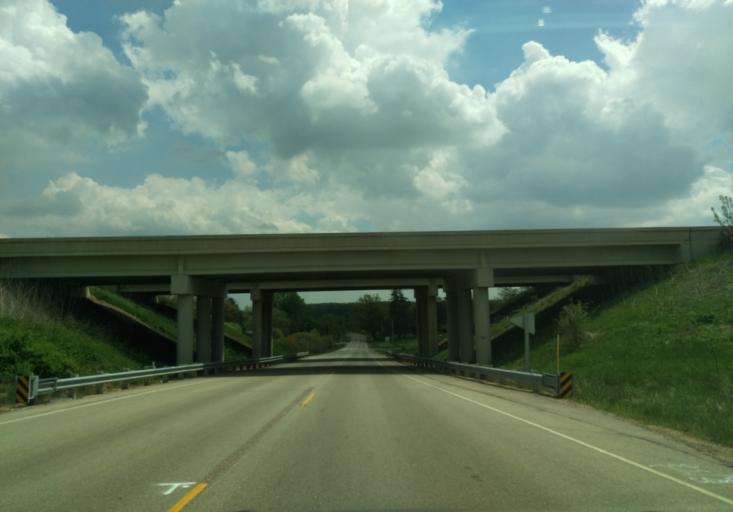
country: US
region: Wisconsin
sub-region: Dane County
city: Mount Horeb
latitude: 42.9979
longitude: -89.7201
